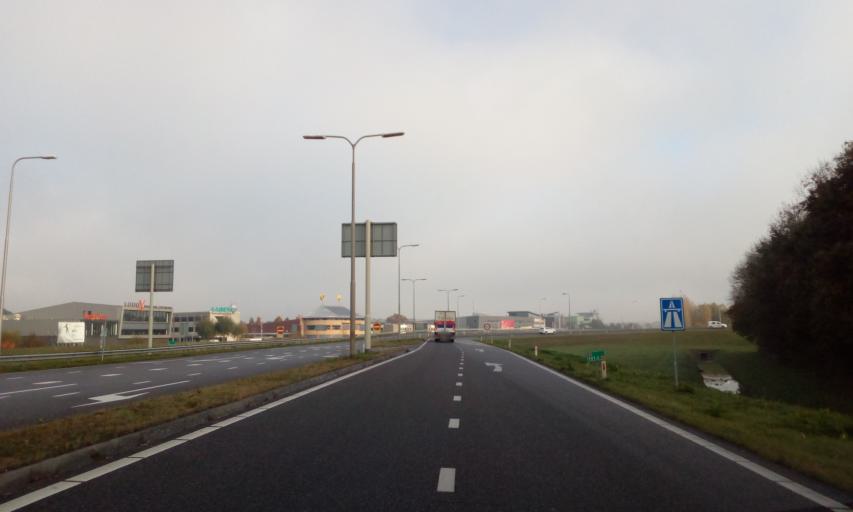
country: NL
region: Gelderland
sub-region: Gemeente Lochem
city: Epse
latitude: 52.2371
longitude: 6.2121
